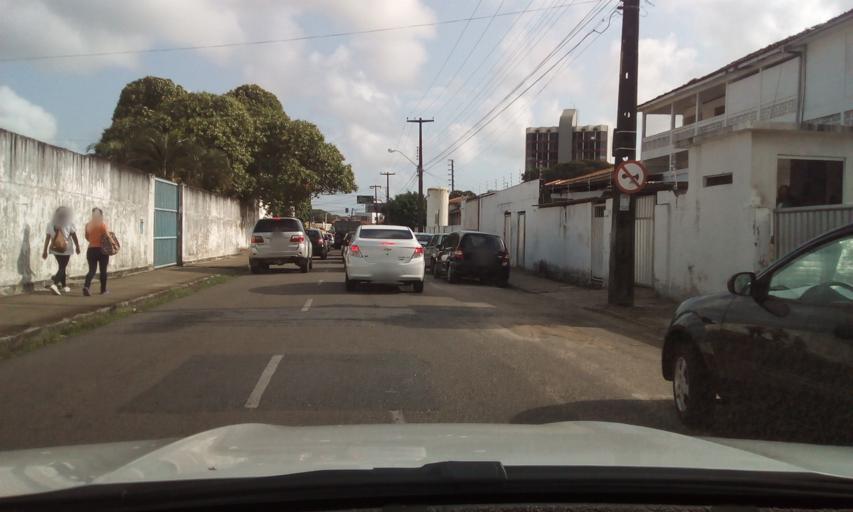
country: BR
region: Paraiba
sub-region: Joao Pessoa
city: Joao Pessoa
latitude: -7.1277
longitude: -34.8740
